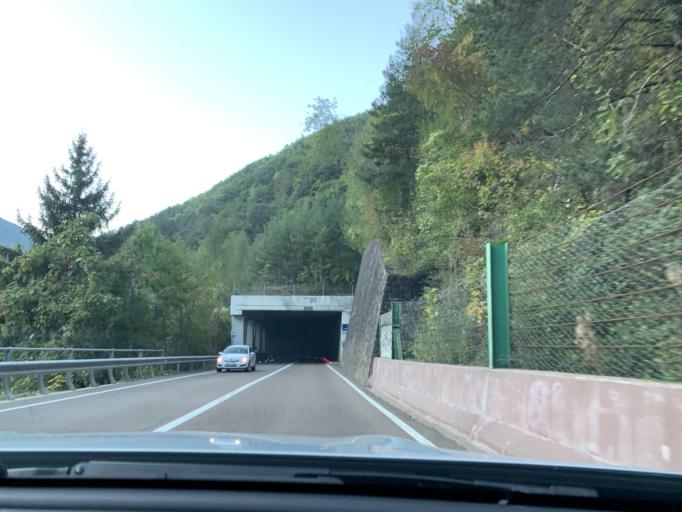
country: IT
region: Trentino-Alto Adige
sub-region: Bolzano
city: Cornedo All'Isarco
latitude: 46.4572
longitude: 11.4273
